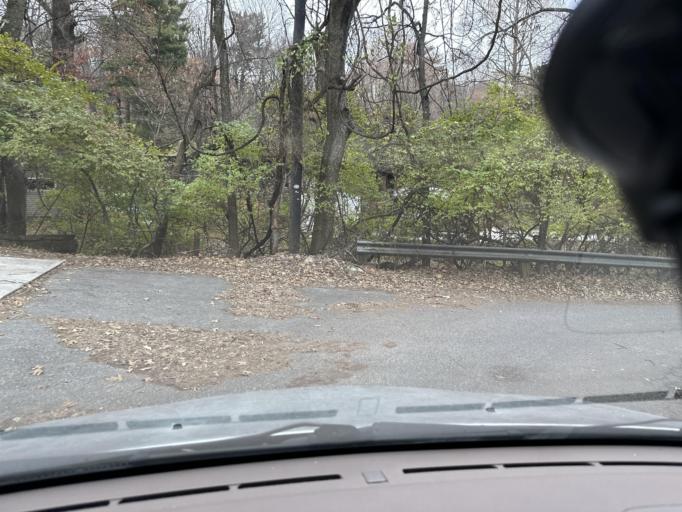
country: US
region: Arkansas
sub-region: Washington County
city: Fayetteville
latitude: 36.0652
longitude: -94.1548
